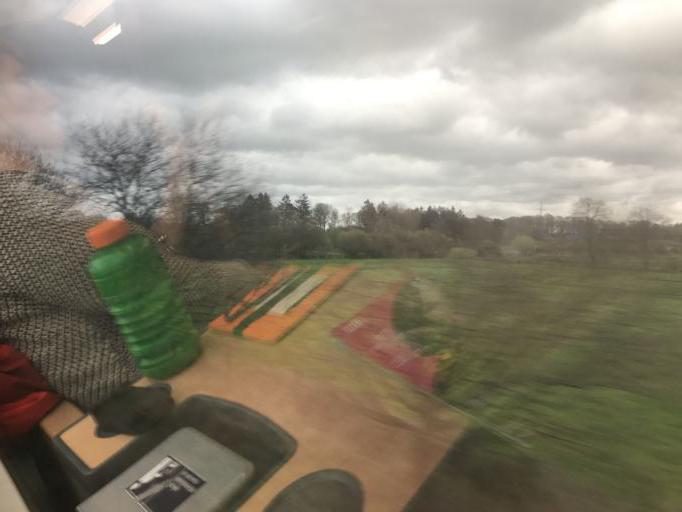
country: DE
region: Schleswig-Holstein
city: Brokstedt
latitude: 53.9834
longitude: 9.8109
